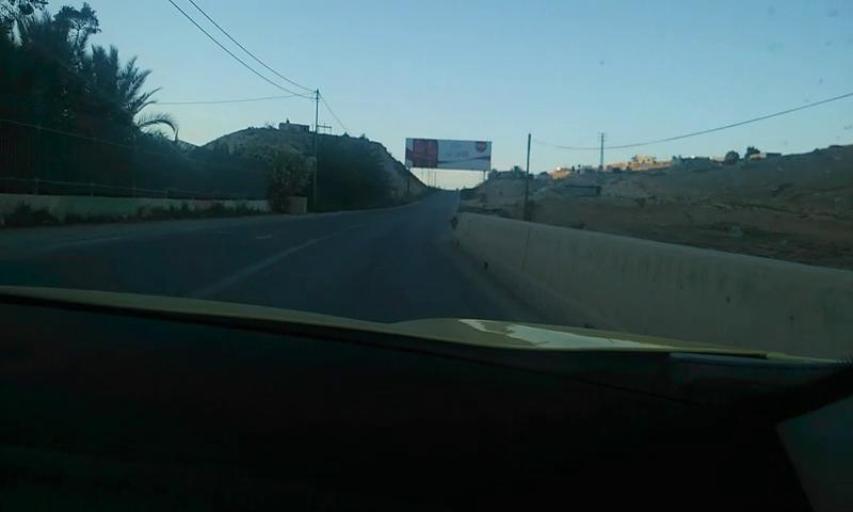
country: PS
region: West Bank
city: An Nuway`imah
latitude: 31.9005
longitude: 35.4271
